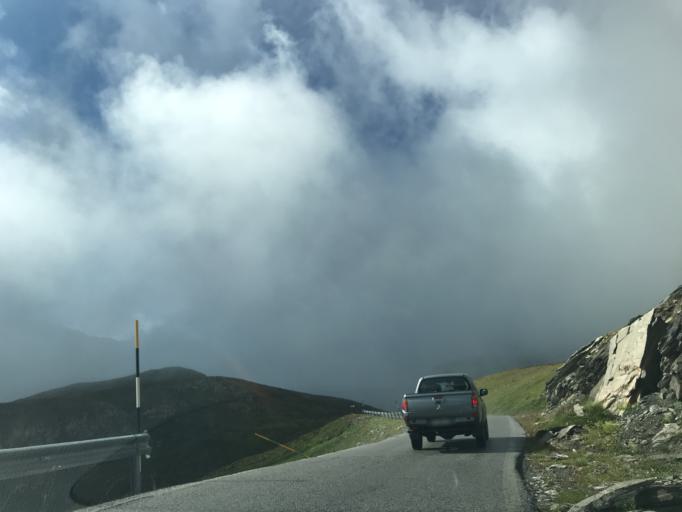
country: IT
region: Piedmont
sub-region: Provincia di Cuneo
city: Pontechianale
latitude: 44.6754
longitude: 6.9911
